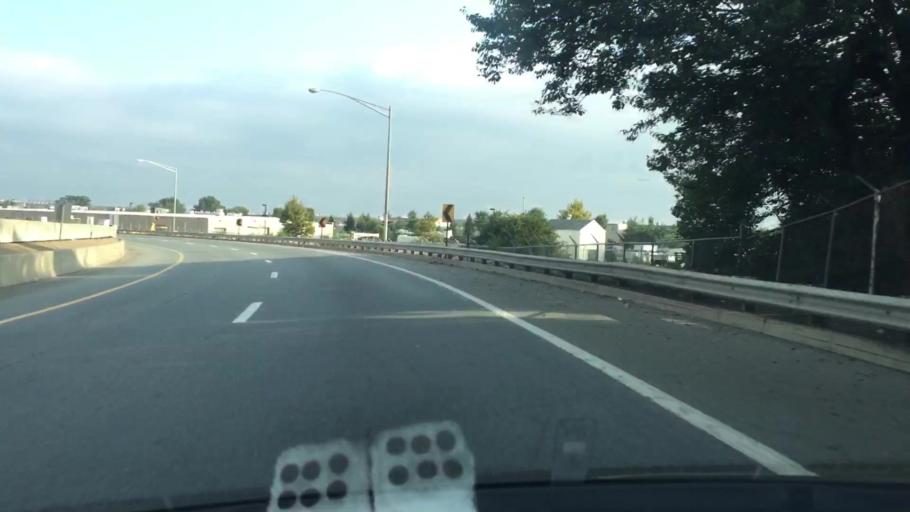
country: US
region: Pennsylvania
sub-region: Philadelphia County
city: Philadelphia
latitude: 39.9150
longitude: -75.1901
